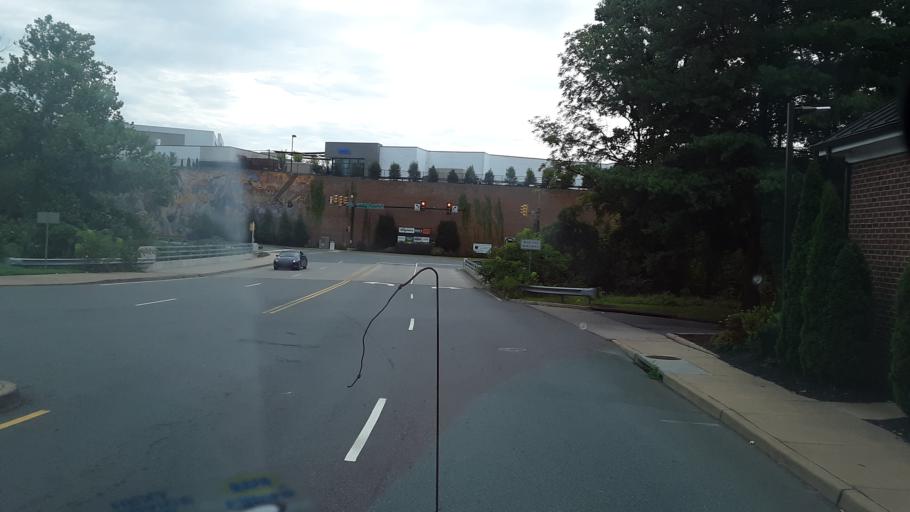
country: US
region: Virginia
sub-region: City of Charlottesville
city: Charlottesville
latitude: 38.0118
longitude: -78.5019
